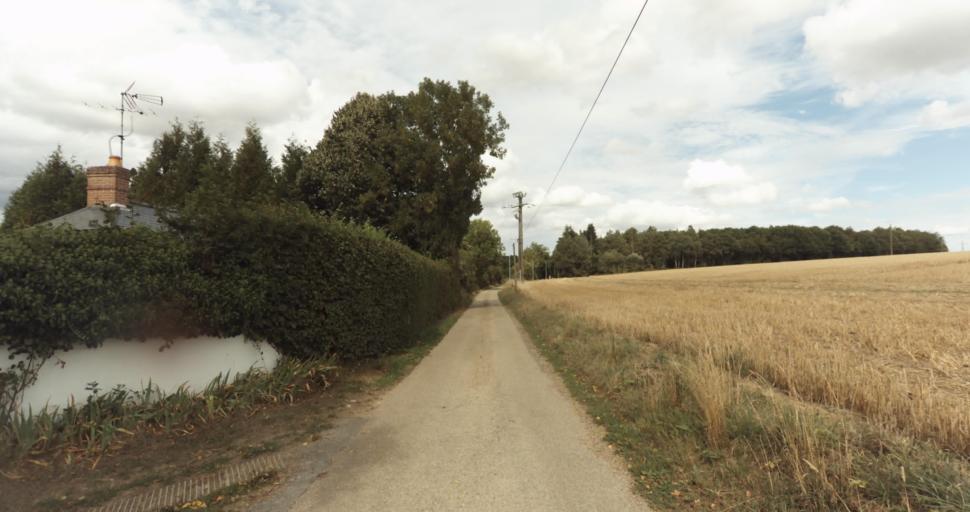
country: FR
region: Lower Normandy
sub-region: Departement de l'Orne
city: Gace
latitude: 48.8936
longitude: 0.3635
